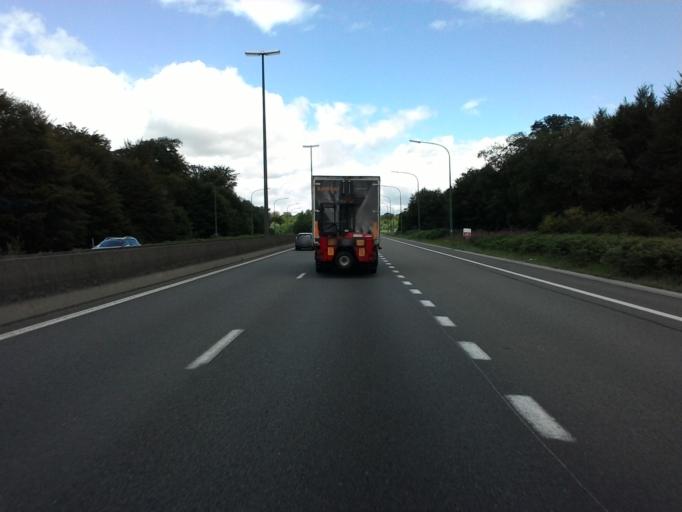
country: BE
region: Wallonia
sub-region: Province du Luxembourg
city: Habay-la-Vieille
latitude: 49.7435
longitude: 5.5723
